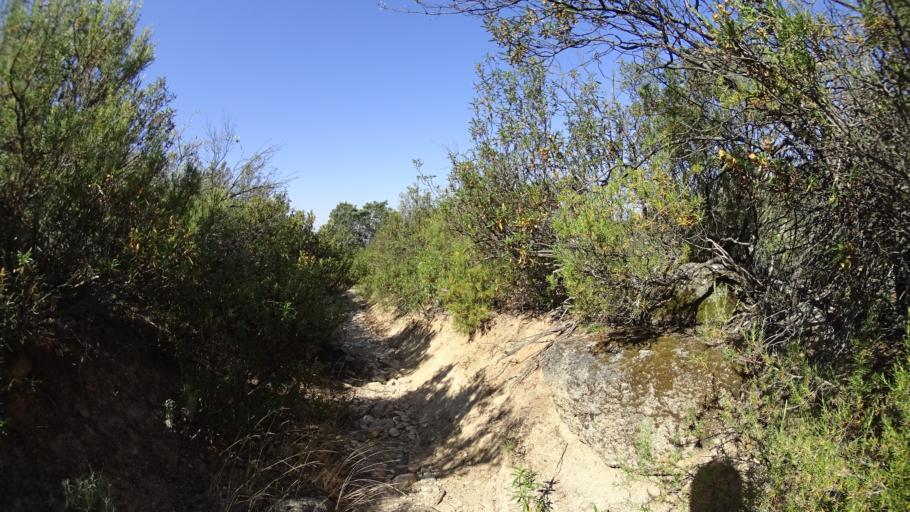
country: ES
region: Madrid
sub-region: Provincia de Madrid
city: Hoyo de Manzanares
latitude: 40.6423
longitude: -3.9360
